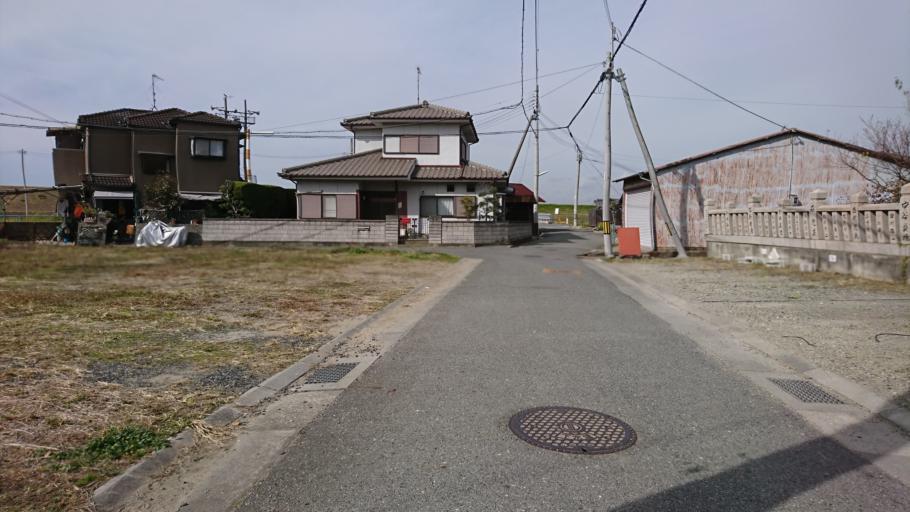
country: JP
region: Hyogo
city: Kakogawacho-honmachi
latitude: 34.7491
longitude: 134.8134
